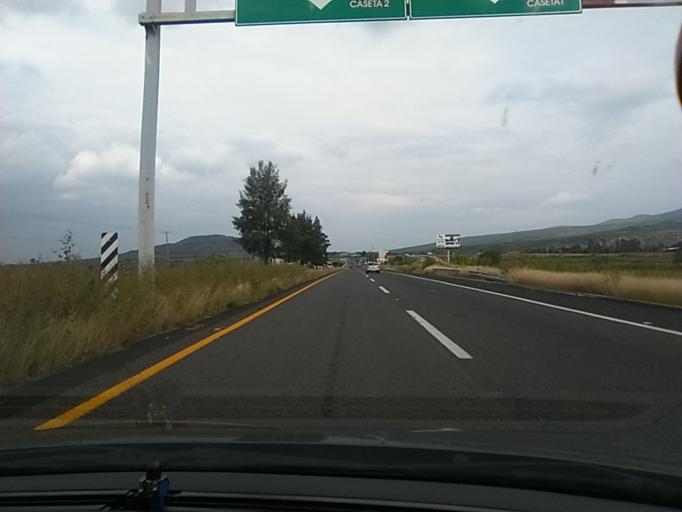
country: MX
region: Michoacan
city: Ecuandureo
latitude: 20.1752
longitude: -102.1961
